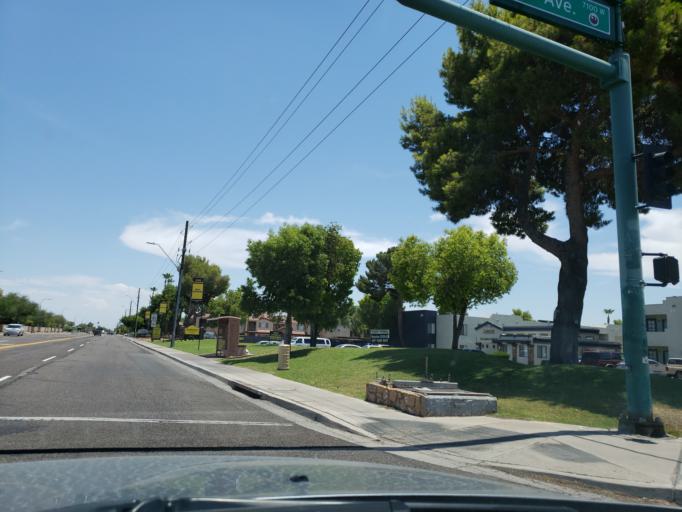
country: US
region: Arizona
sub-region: Maricopa County
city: Tolleson
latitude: 33.4654
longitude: -112.2108
